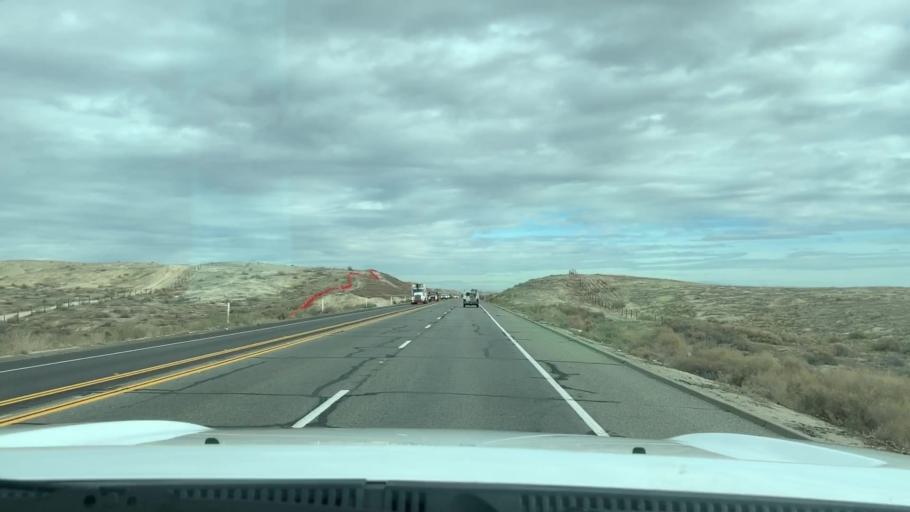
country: US
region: California
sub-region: Kern County
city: Ford City
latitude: 35.2476
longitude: -119.3443
